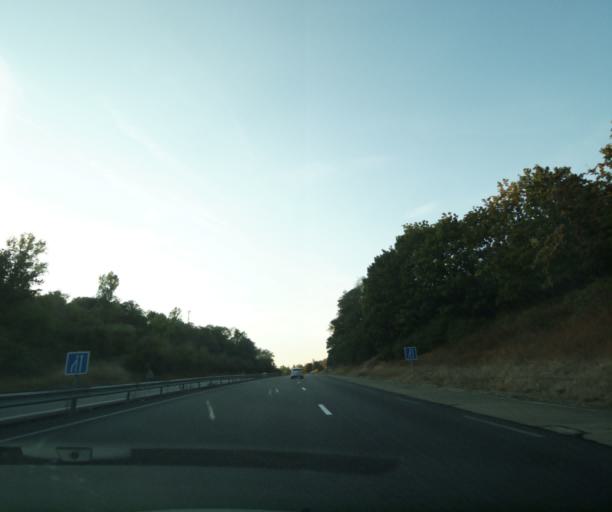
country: FR
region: Aquitaine
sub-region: Departement du Lot-et-Garonne
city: Boe
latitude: 44.1422
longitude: 0.6351
